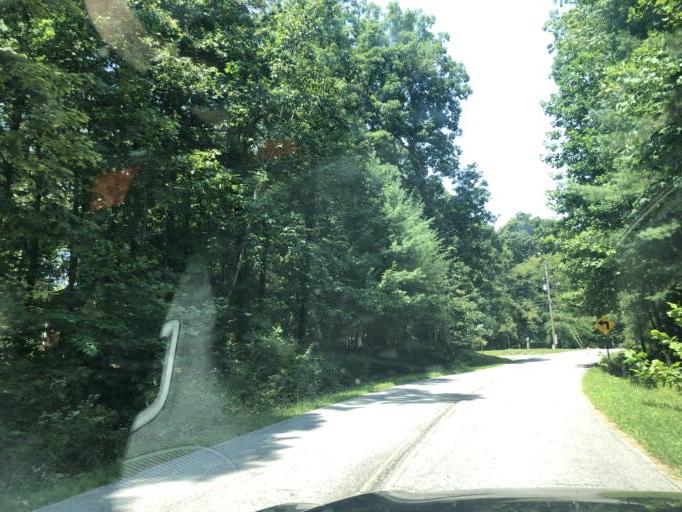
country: US
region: Tennessee
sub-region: Franklin County
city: Sewanee
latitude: 35.2046
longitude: -85.9283
